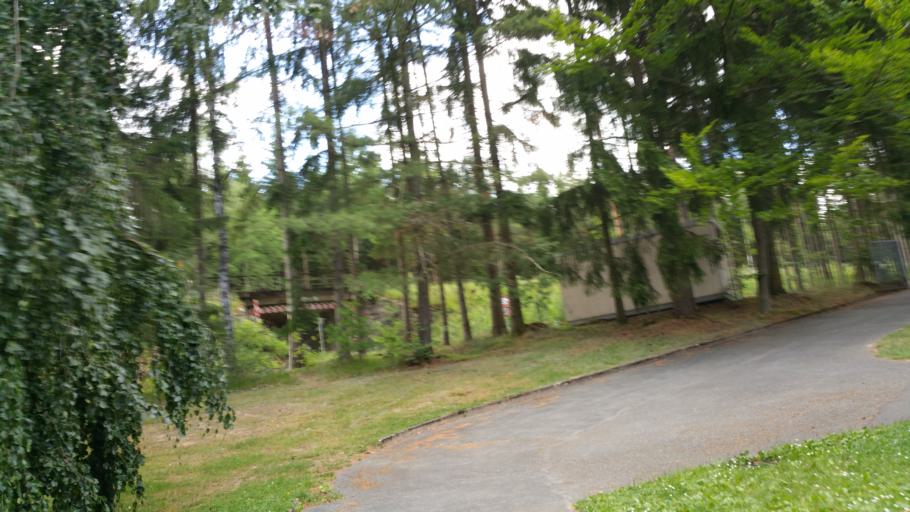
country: DE
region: Bavaria
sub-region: Upper Franconia
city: Schwarzenbach an der Saale
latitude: 50.1991
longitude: 11.9572
